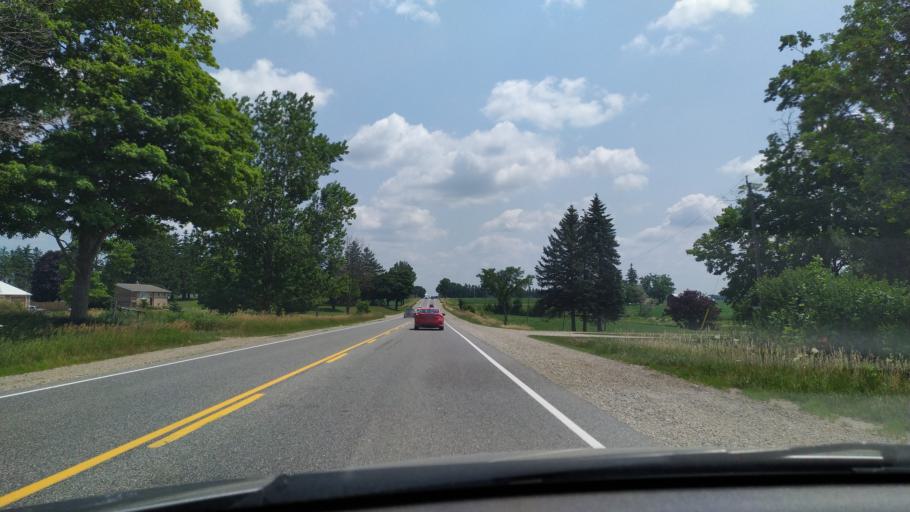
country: CA
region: Ontario
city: Stratford
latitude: 43.3692
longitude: -80.7948
